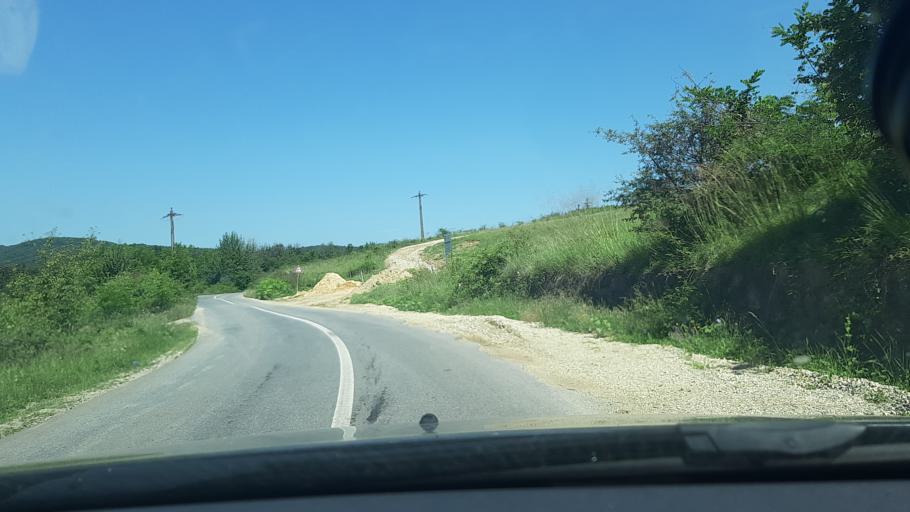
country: RO
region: Hunedoara
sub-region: Comuna Teliucu Inferior
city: Teliucu Inferior
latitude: 45.6942
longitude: 22.8760
